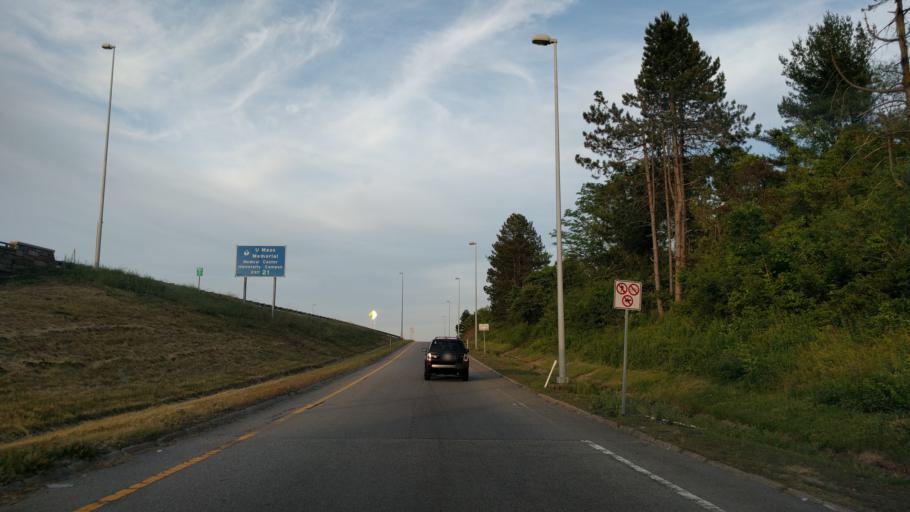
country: US
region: Massachusetts
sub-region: Worcester County
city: Worcester
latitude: 42.2900
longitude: -71.7848
